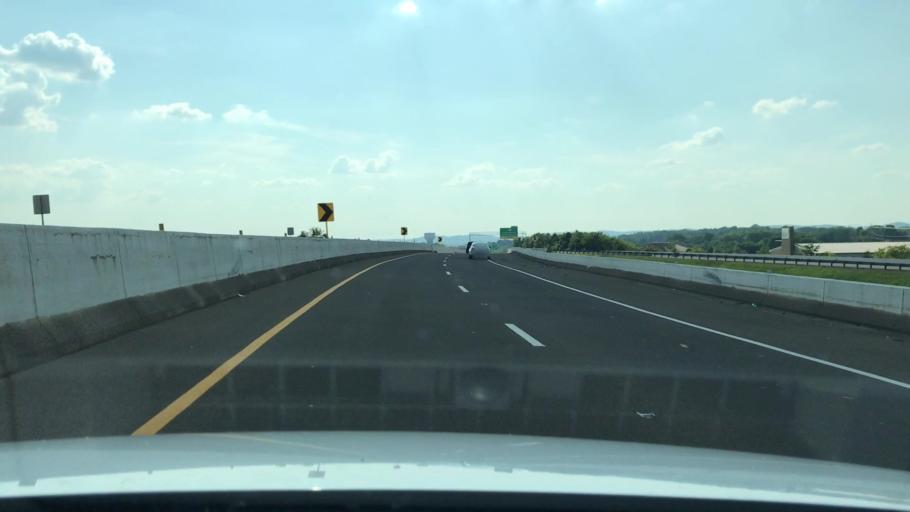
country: US
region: Tennessee
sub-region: Sumner County
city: Hendersonville
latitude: 36.3287
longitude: -86.5572
